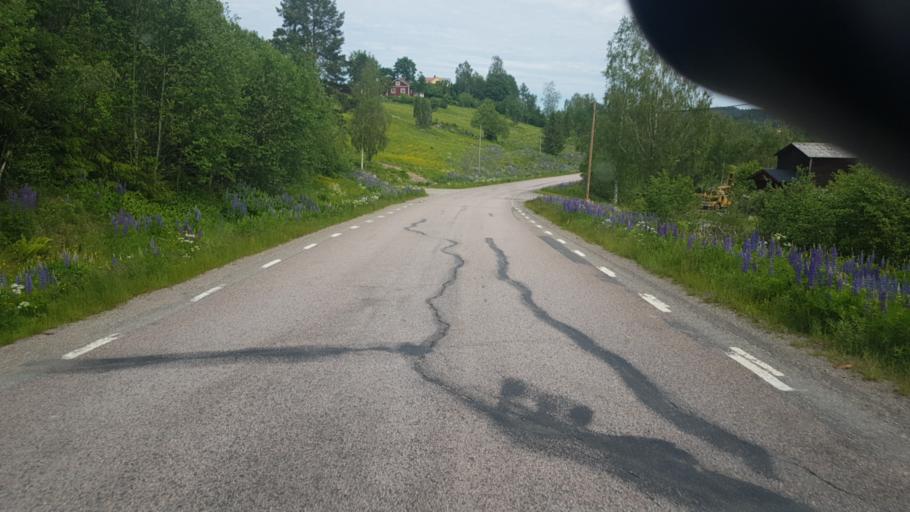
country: SE
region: Vaermland
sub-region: Eda Kommun
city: Amotfors
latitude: 59.8771
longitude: 12.5107
